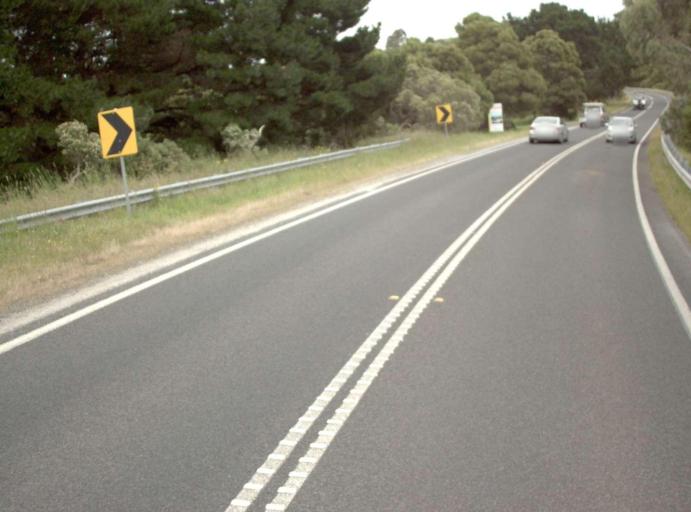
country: AU
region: Victoria
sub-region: Latrobe
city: Morwell
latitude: -38.6321
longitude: 146.1865
